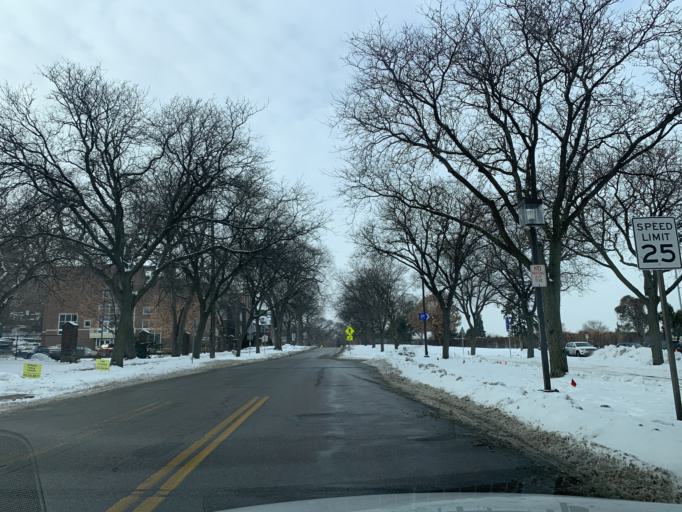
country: US
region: Minnesota
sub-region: Hennepin County
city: Minneapolis
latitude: 44.9699
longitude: -93.2912
